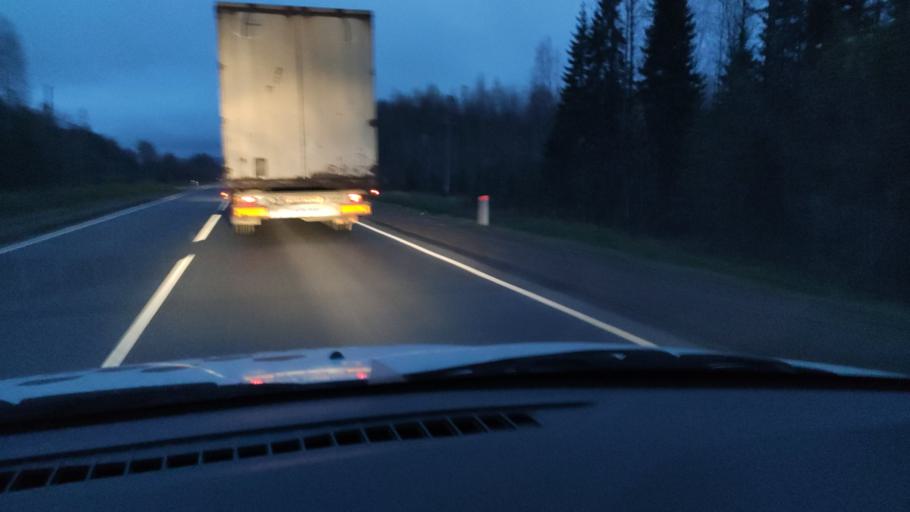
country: RU
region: Kirov
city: Kostino
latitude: 58.8325
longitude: 53.5091
